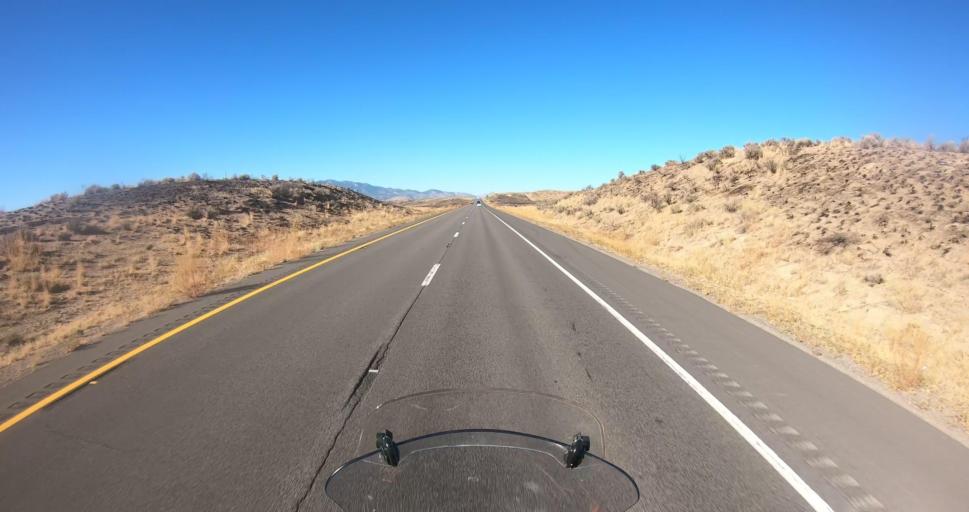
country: US
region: Nevada
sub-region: Washoe County
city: Cold Springs
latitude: 39.7504
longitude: -120.0387
